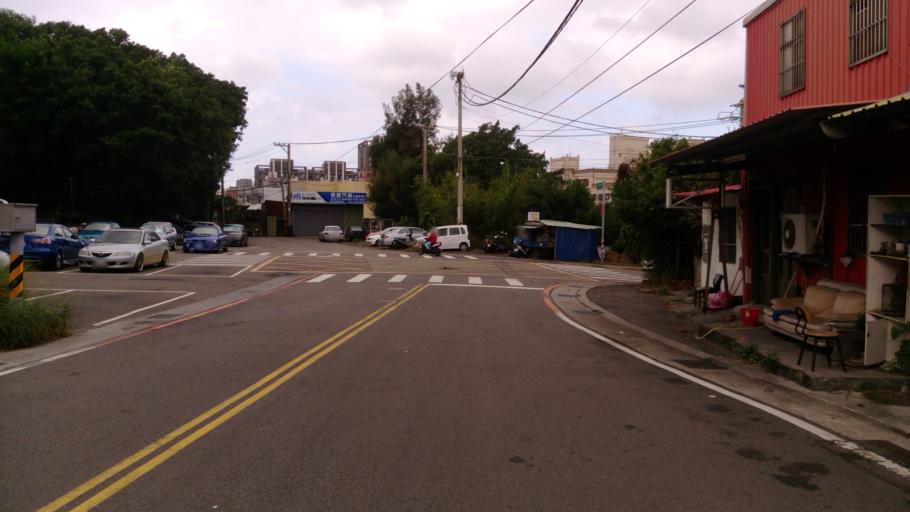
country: TW
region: Taiwan
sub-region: Hsinchu
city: Hsinchu
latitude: 24.7929
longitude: 120.9531
